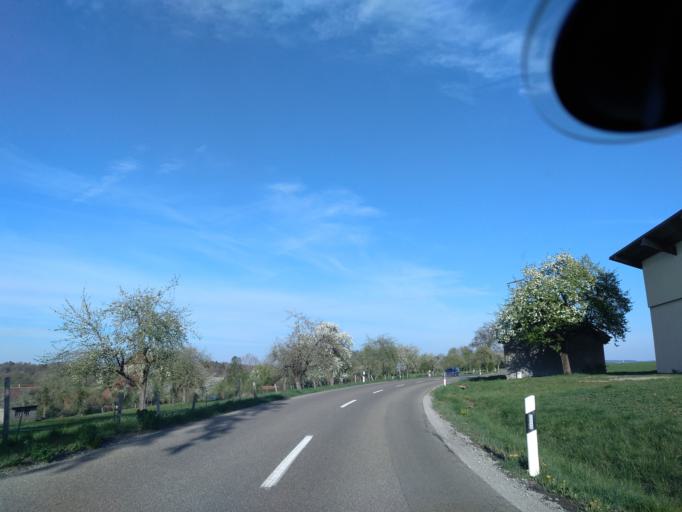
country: DE
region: Baden-Wuerttemberg
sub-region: Regierungsbezirk Stuttgart
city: Blaufelden
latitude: 49.2514
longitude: 9.9482
